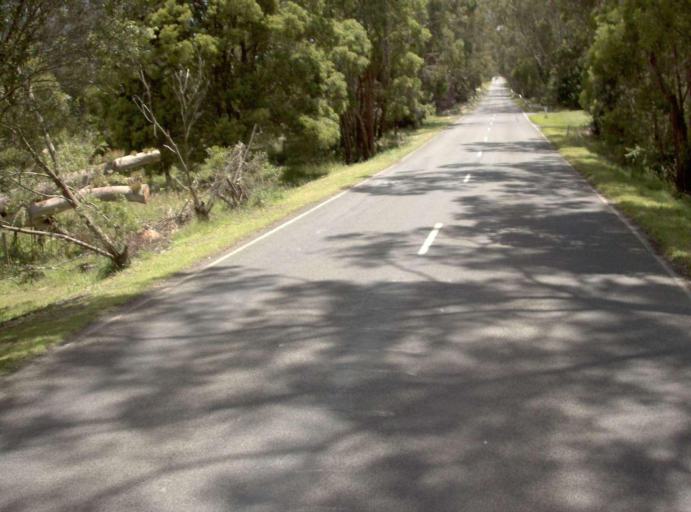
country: AU
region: Victoria
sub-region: Bass Coast
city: North Wonthaggi
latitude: -38.6041
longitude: 146.0184
